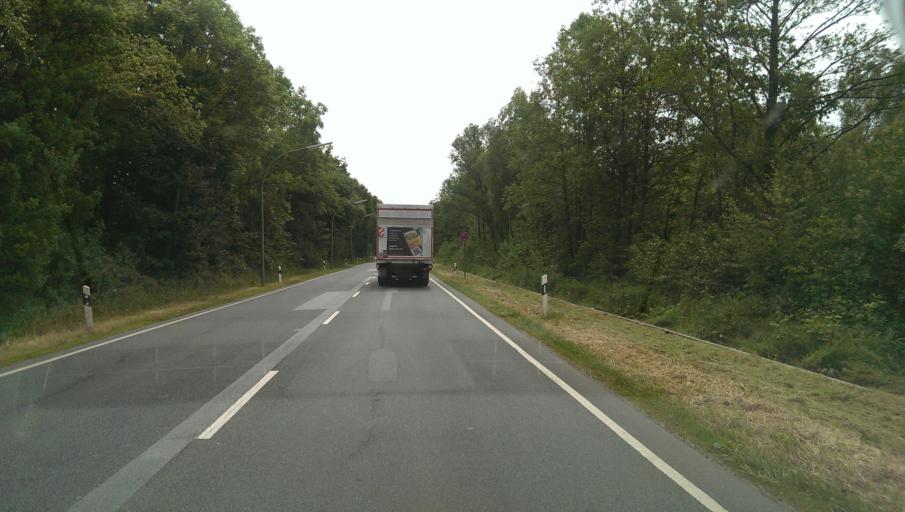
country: DE
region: Bremen
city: Bremerhaven
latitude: 53.5818
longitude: 8.5723
